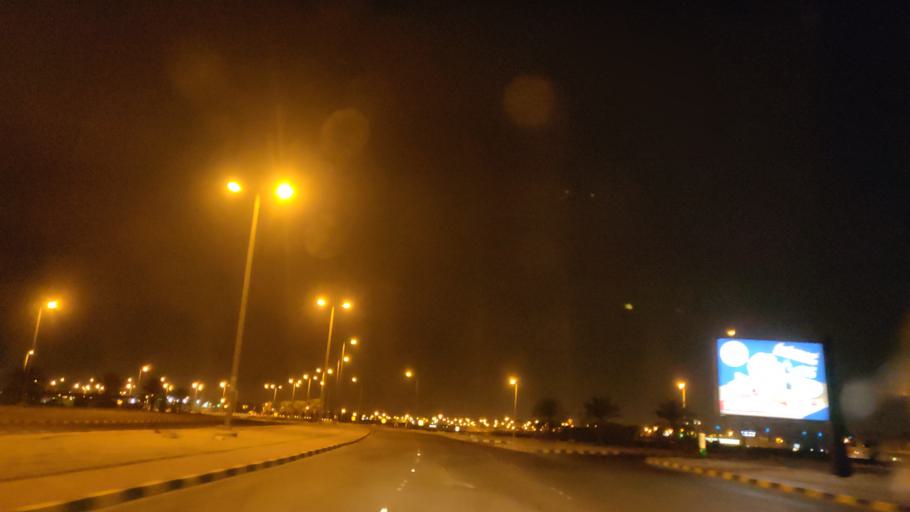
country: KW
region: Al Farwaniyah
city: Al Farwaniyah
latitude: 29.2589
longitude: 47.9587
